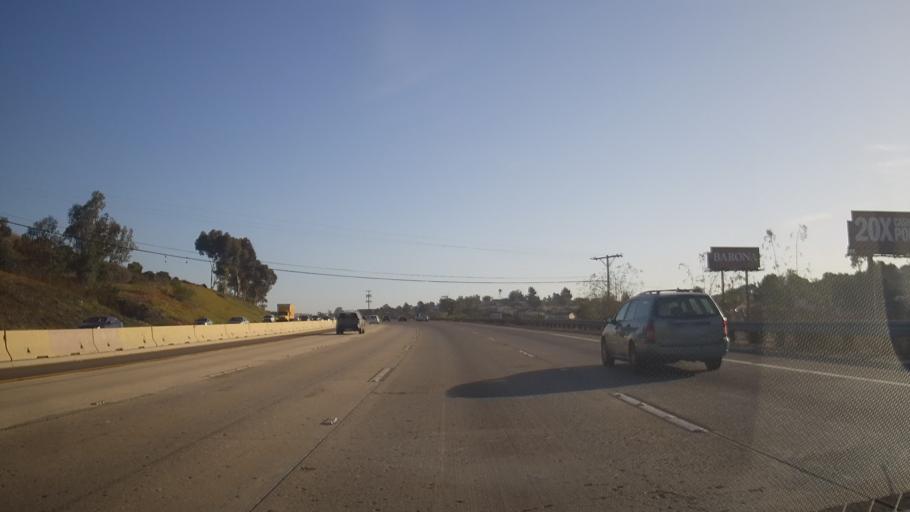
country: US
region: California
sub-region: San Diego County
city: Lemon Grove
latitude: 32.7293
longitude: -117.0655
